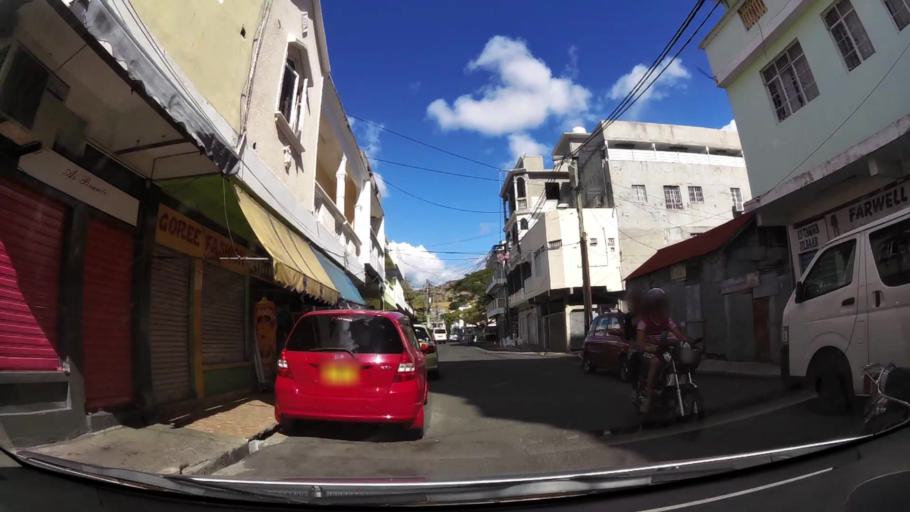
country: MU
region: Port Louis
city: Port Louis
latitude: -20.1622
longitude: 57.5158
